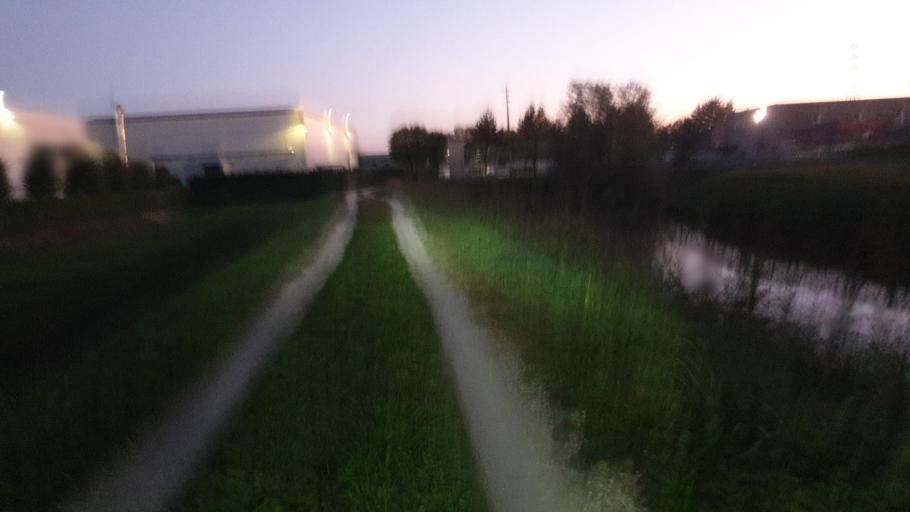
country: IT
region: Veneto
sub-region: Provincia di Venezia
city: Fiesso d'Artico
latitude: 45.4241
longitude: 12.0193
